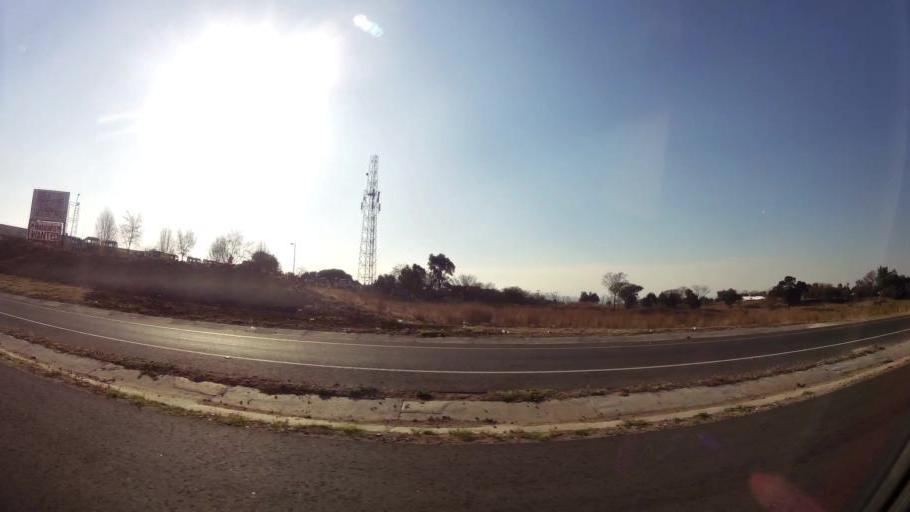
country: ZA
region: Gauteng
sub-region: West Rand District Municipality
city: Muldersdriseloop
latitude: -26.0172
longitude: 27.8673
